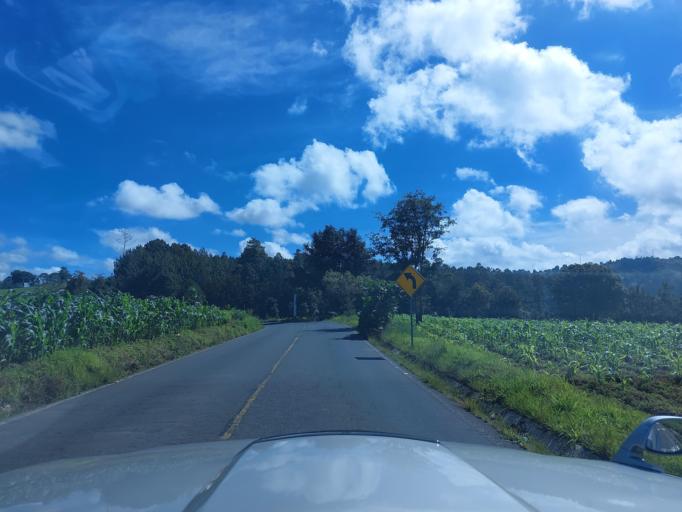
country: GT
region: Chimaltenango
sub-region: Municipio de Santa Cruz Balanya
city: Santa Cruz Balanya
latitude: 14.7044
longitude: -90.8974
